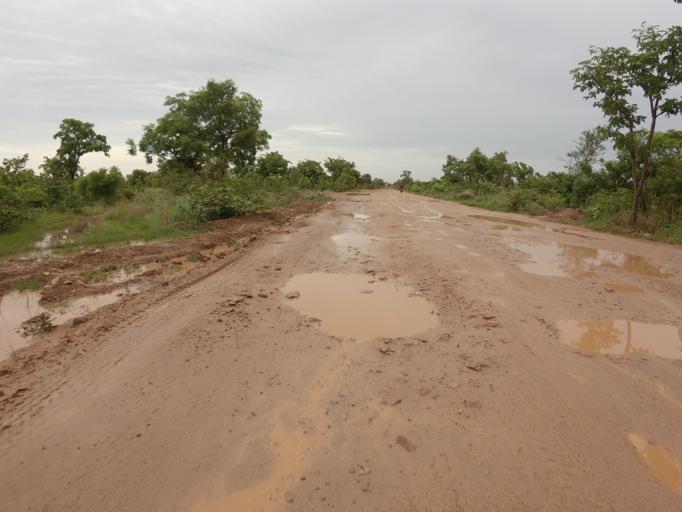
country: GH
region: Upper East
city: Bolgatanga
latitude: 10.8783
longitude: -0.6330
